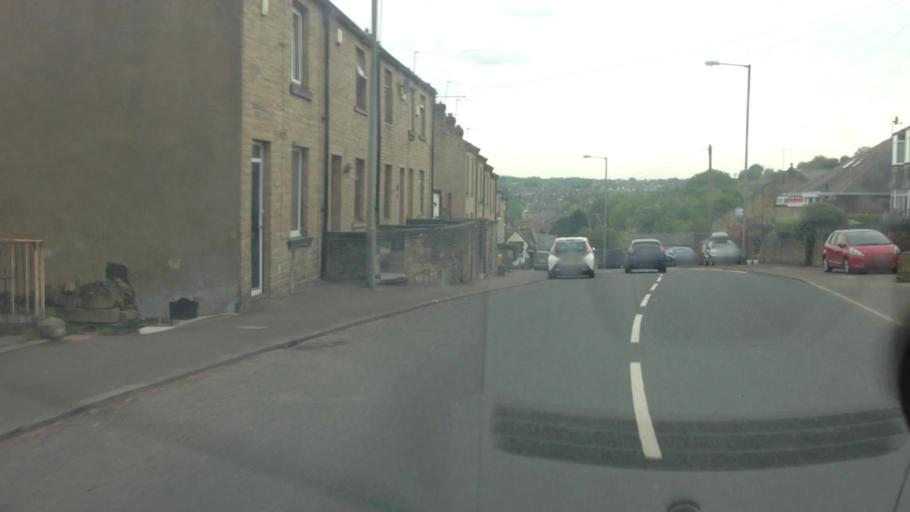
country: GB
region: England
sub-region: Calderdale
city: Brighouse
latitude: 53.6925
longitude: -1.7907
